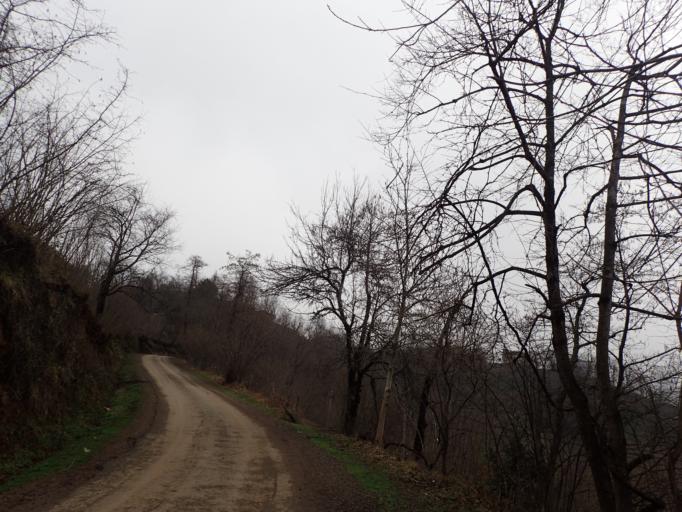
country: TR
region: Ordu
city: Camas
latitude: 40.9200
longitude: 37.5636
